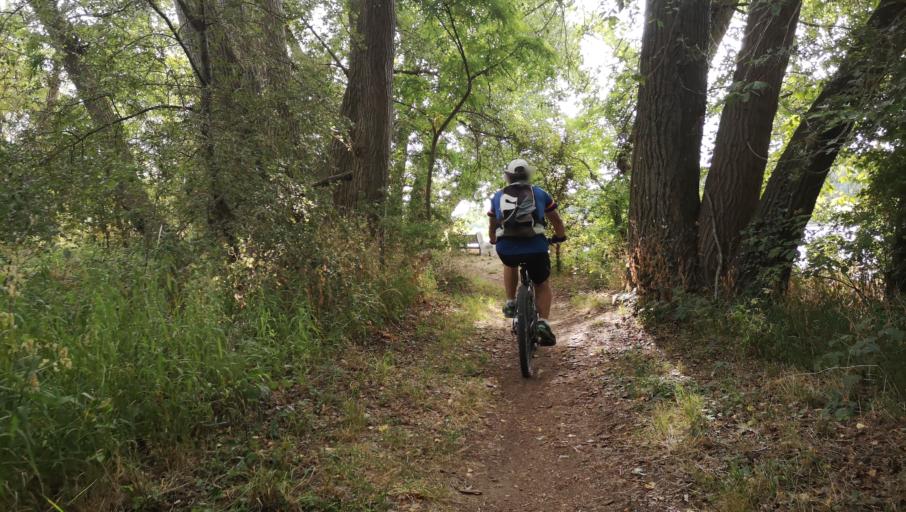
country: FR
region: Centre
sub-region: Departement du Loiret
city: Sandillon
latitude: 47.8567
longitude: 2.0408
